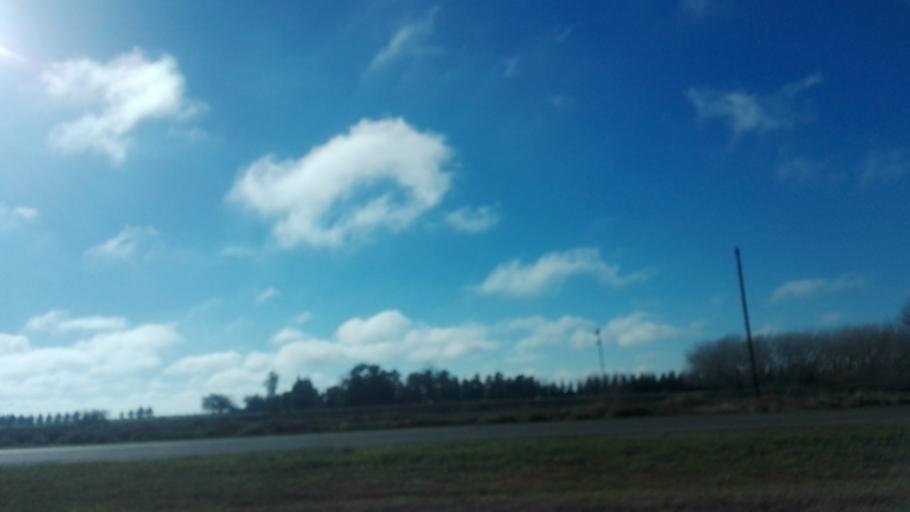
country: AR
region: Buenos Aires
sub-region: Partido de Castelli
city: Castelli
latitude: -35.8384
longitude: -57.9109
